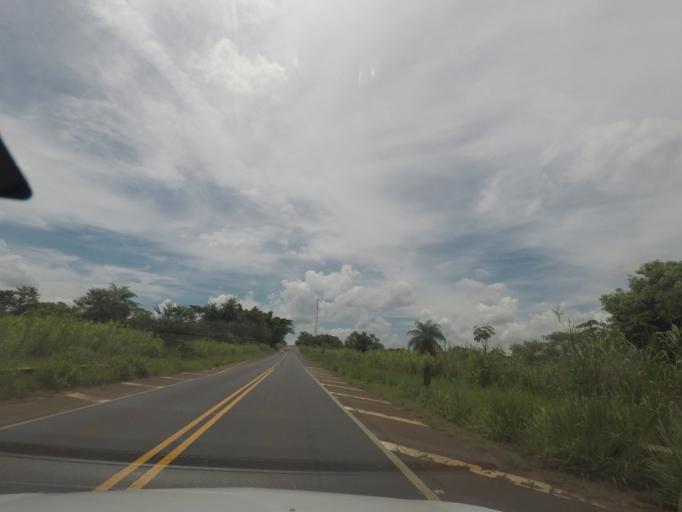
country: BR
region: Sao Paulo
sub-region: Barretos
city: Barretos
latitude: -20.4265
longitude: -48.6289
